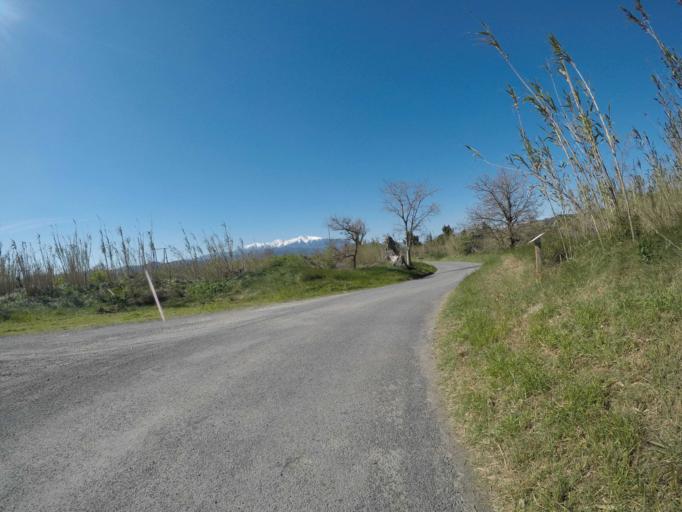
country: FR
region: Languedoc-Roussillon
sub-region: Departement des Pyrenees-Orientales
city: Millas
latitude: 42.6989
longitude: 2.6656
